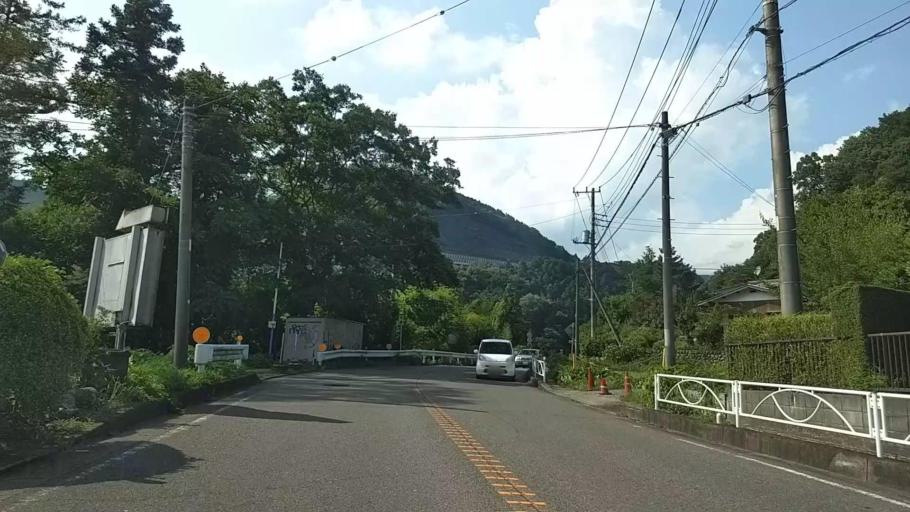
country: JP
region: Yamanashi
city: Uenohara
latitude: 35.6221
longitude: 139.2041
